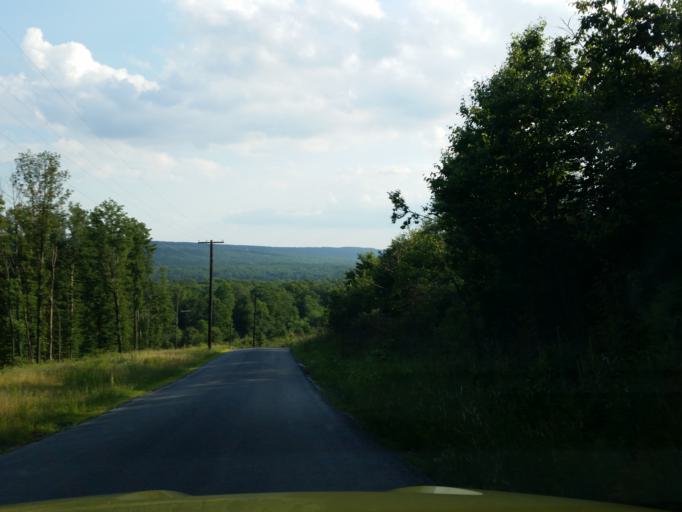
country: US
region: Pennsylvania
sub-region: Dauphin County
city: Williamstown
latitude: 40.4586
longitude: -76.6266
